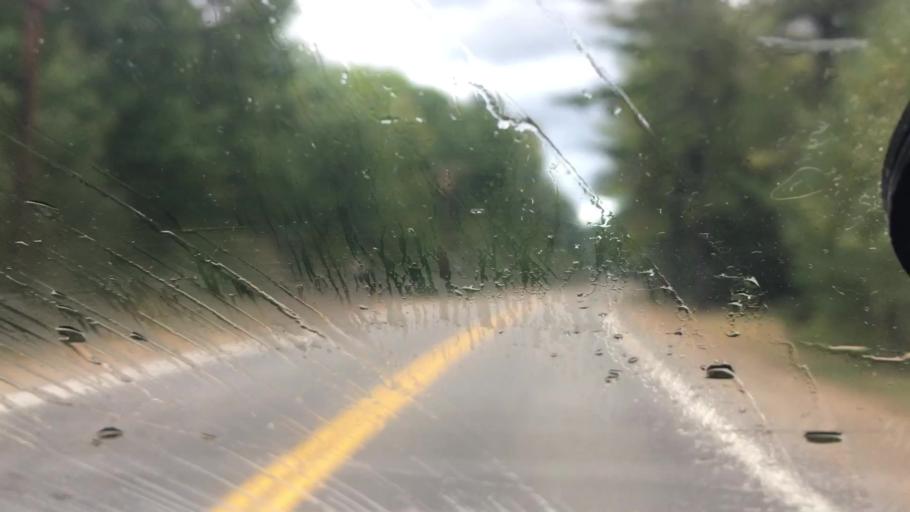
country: US
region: New Hampshire
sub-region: Carroll County
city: Wakefield
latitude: 43.6162
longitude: -71.0004
